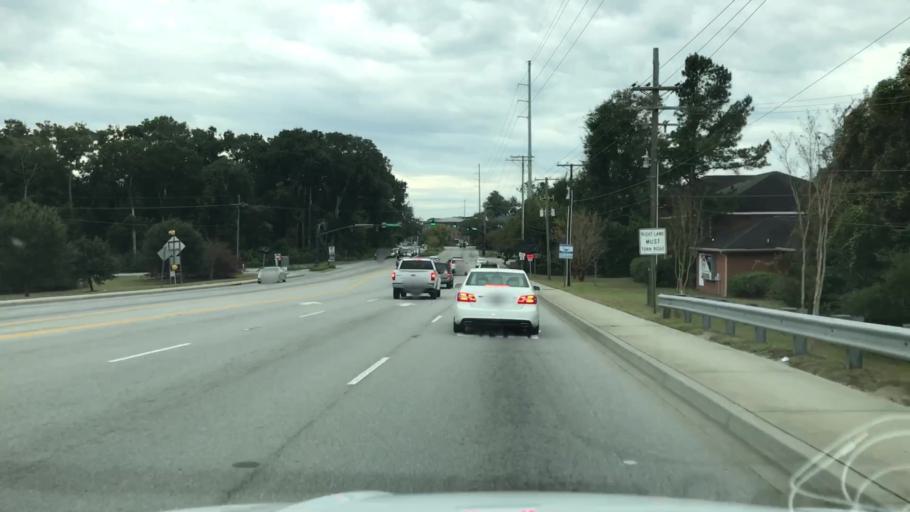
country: US
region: South Carolina
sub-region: Charleston County
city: Charleston
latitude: 32.7647
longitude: -79.9745
